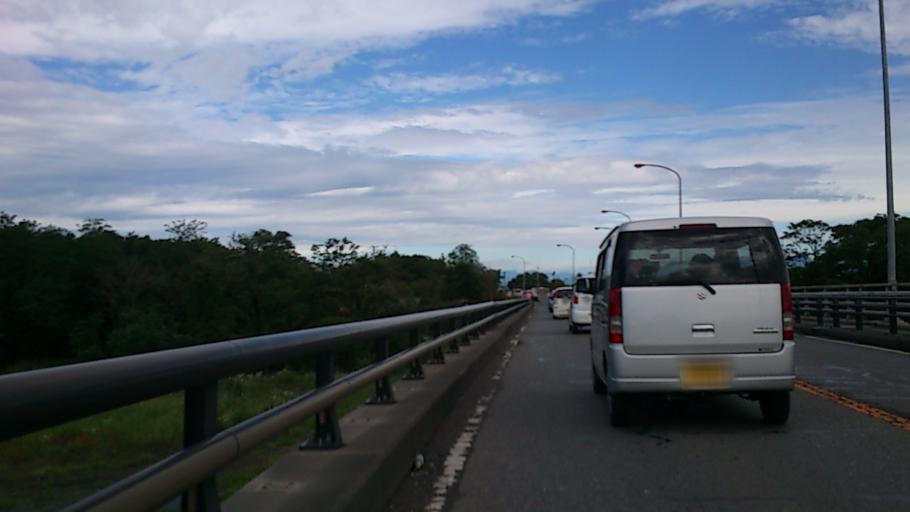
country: JP
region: Gunma
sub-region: Sawa-gun
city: Tamamura
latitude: 36.2681
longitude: 139.1199
